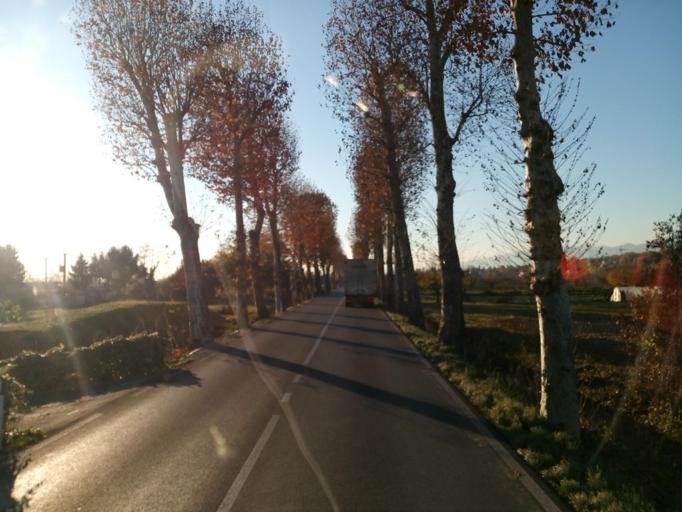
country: IT
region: Veneto
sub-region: Provincia di Treviso
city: Asolo
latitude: 45.7921
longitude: 11.9369
